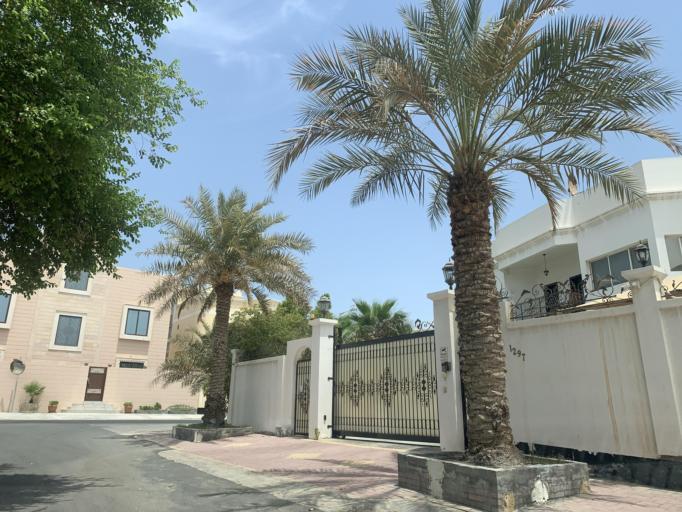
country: BH
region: Northern
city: Madinat `Isa
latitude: 26.1830
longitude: 50.4723
